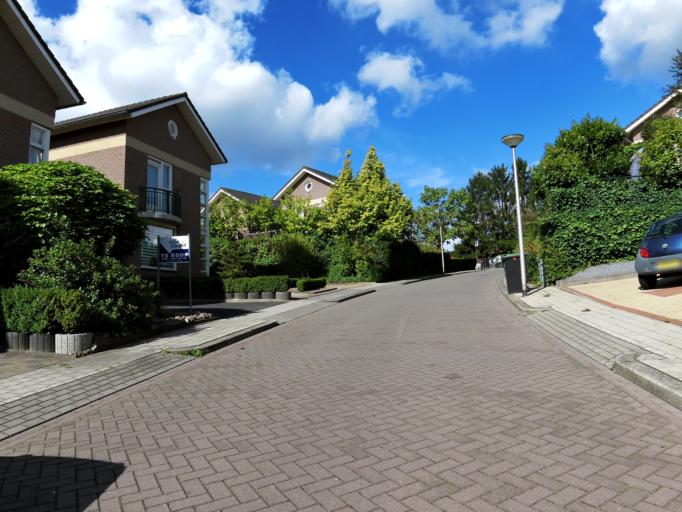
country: NL
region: Limburg
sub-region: Gemeente Kerkrade
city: Kerkrade
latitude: 50.8620
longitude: 6.0416
